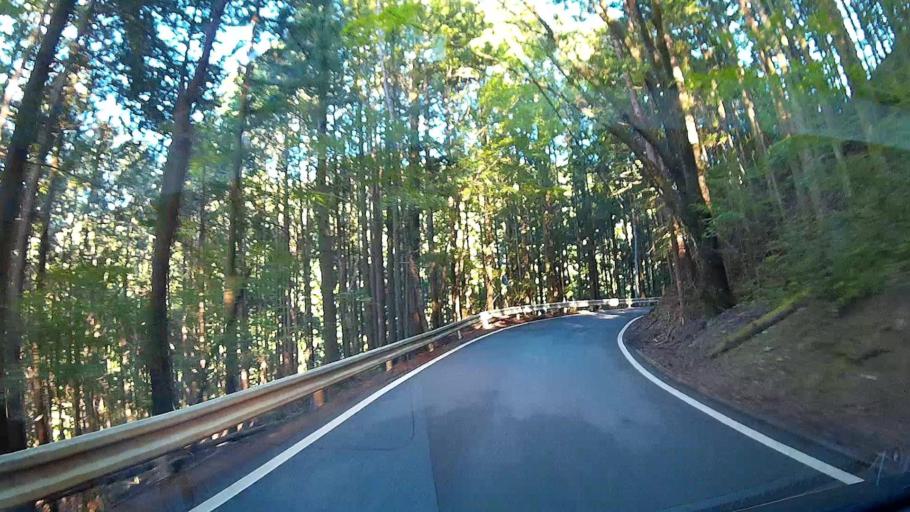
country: JP
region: Shizuoka
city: Shizuoka-shi
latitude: 35.2055
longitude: 138.2300
